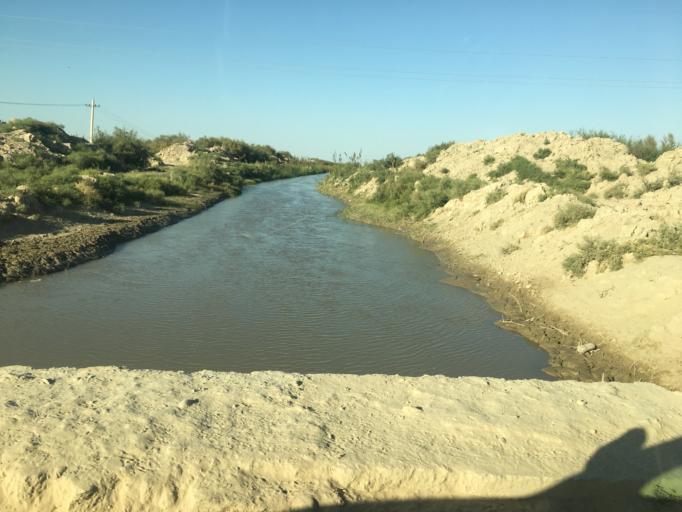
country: IR
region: Razavi Khorasan
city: Sarakhs
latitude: 37.0631
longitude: 61.2595
